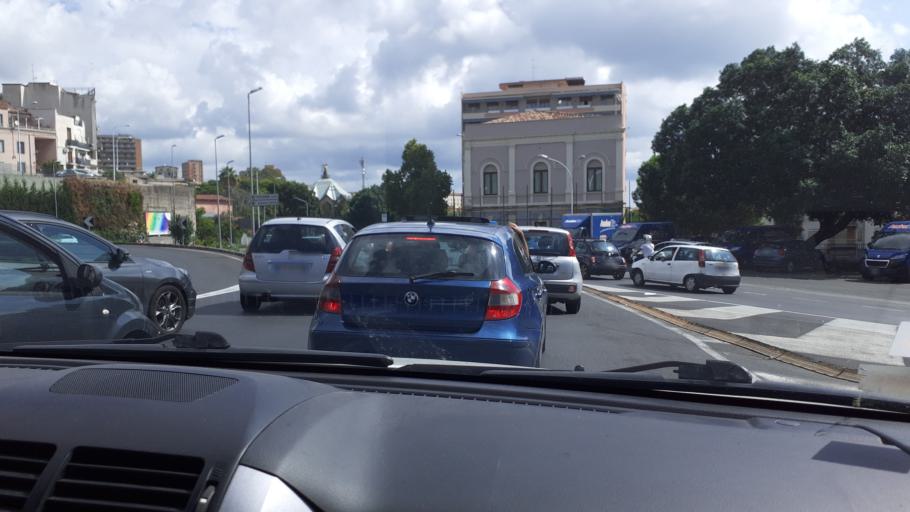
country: IT
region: Sicily
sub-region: Catania
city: Canalicchio
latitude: 37.5263
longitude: 15.0816
